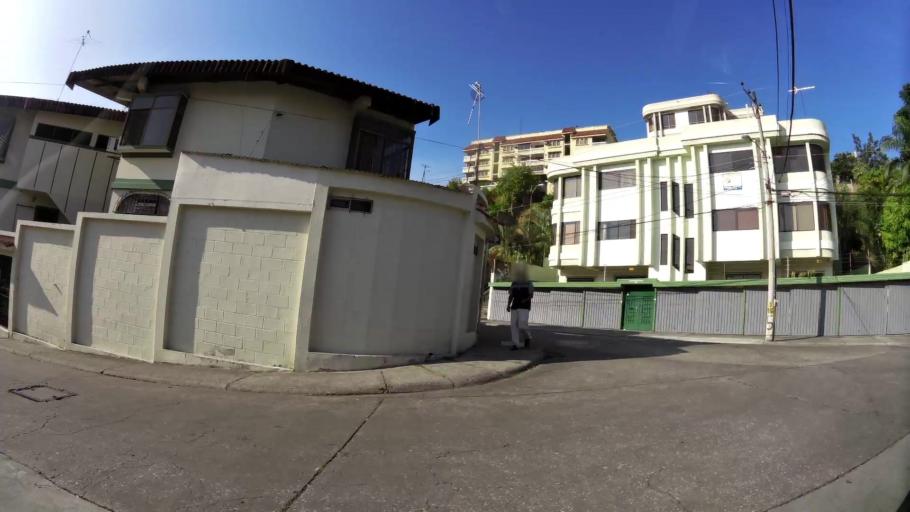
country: EC
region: Guayas
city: Guayaquil
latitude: -2.1622
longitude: -79.9056
